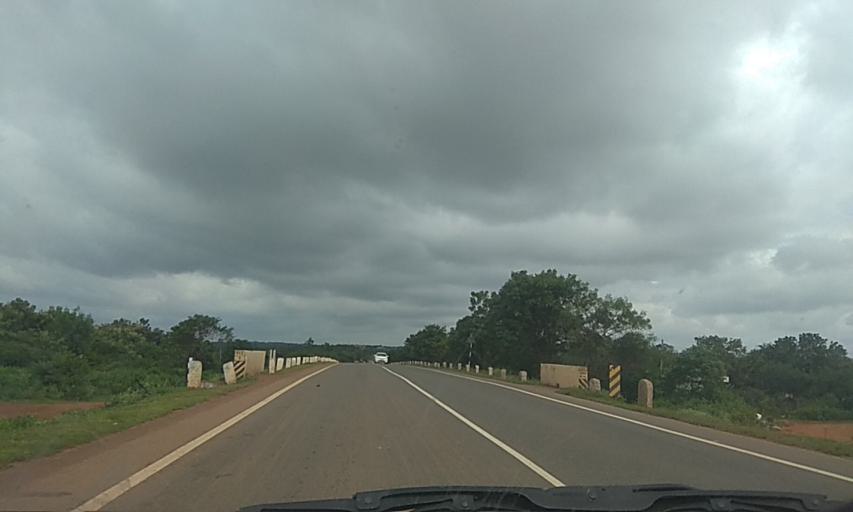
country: IN
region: Karnataka
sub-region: Dharwad
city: Hubli
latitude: 15.3423
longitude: 75.0802
